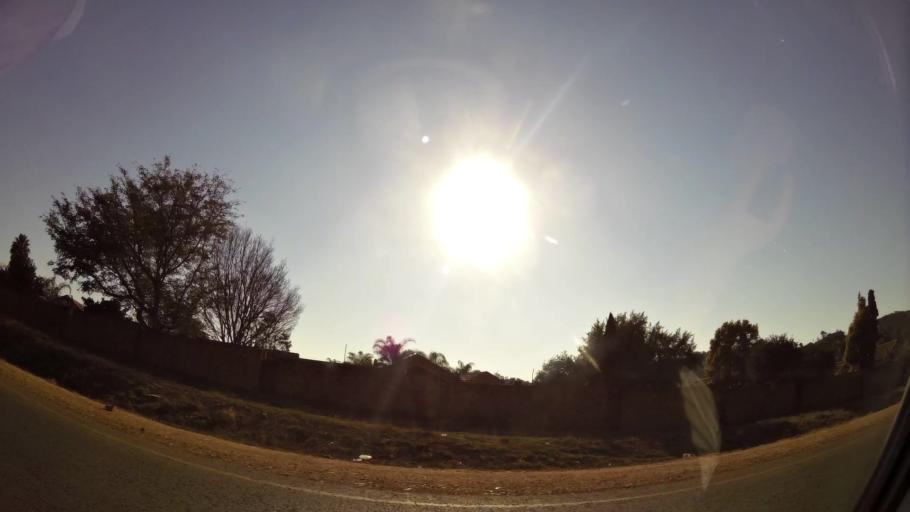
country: ZA
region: Gauteng
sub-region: City of Tshwane Metropolitan Municipality
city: Pretoria
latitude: -25.7845
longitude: 28.3316
